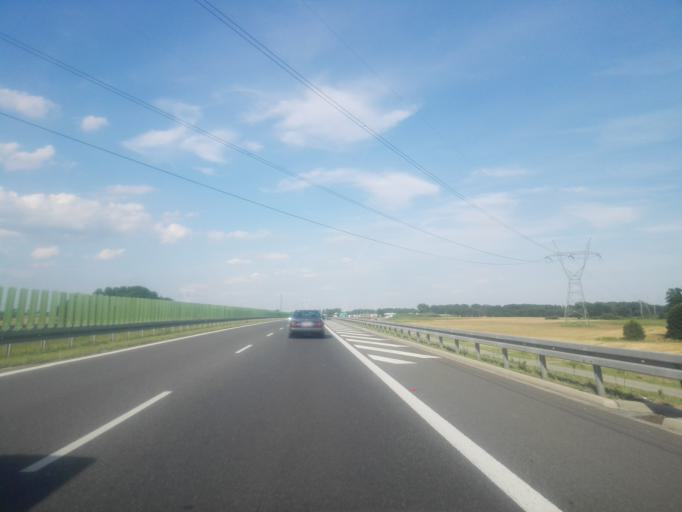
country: PL
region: Lower Silesian Voivodeship
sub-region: Powiat wroclawski
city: Dlugoleka
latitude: 51.2221
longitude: 17.1527
